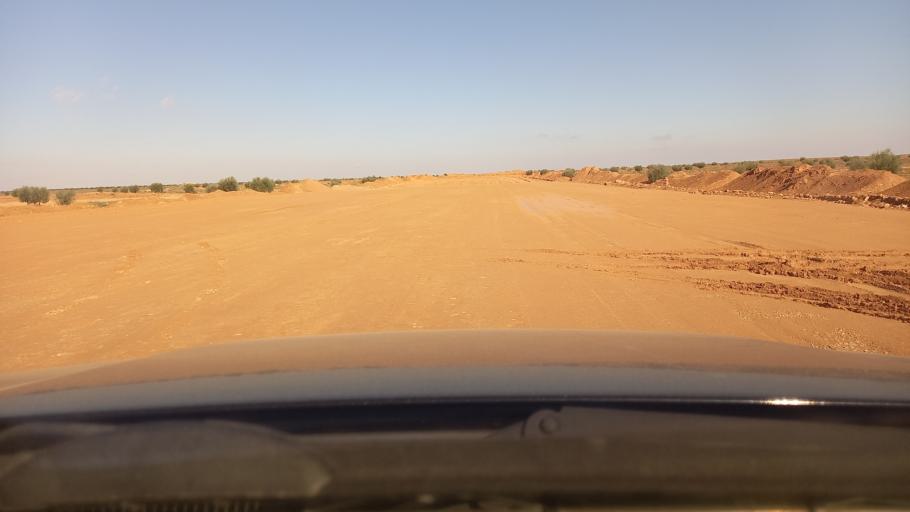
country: TN
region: Madanin
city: Medenine
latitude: 33.1766
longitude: 10.5286
